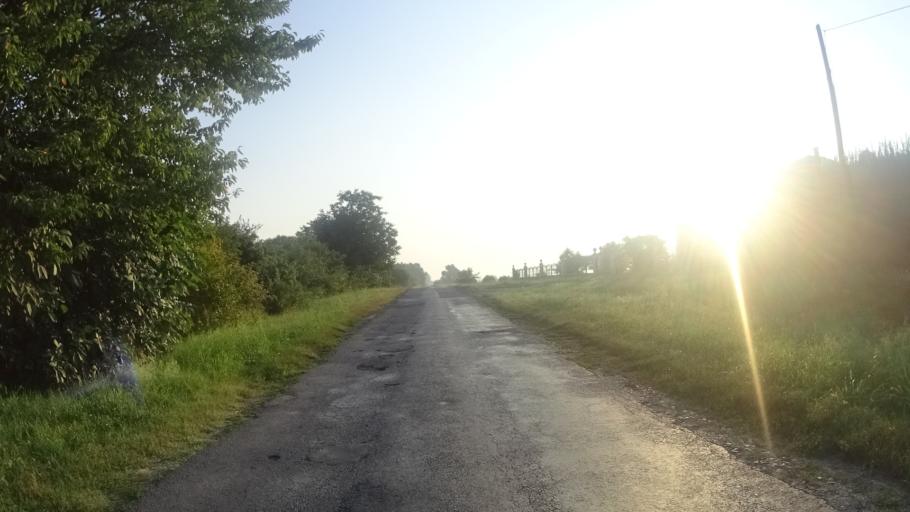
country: HU
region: Zala
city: Zalakomar
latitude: 46.5279
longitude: 17.1349
